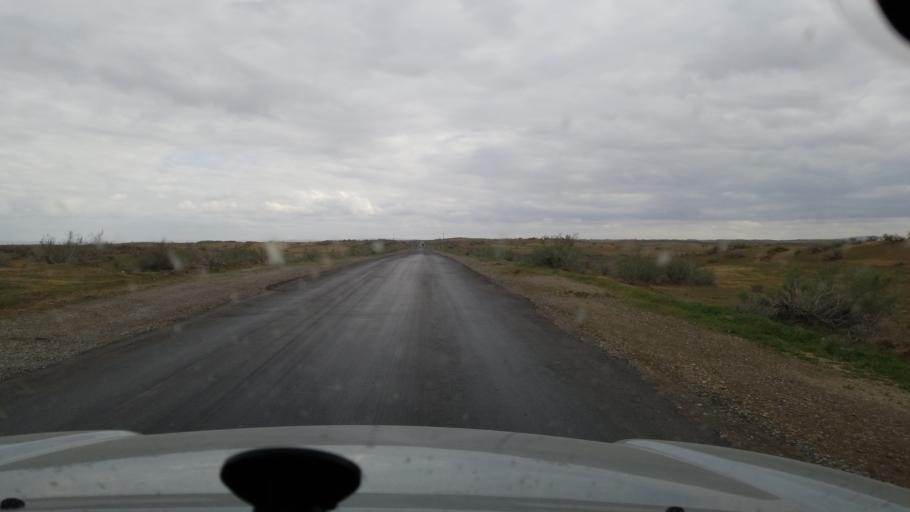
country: TM
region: Mary
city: Serhetabat
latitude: 36.0935
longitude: 62.6116
